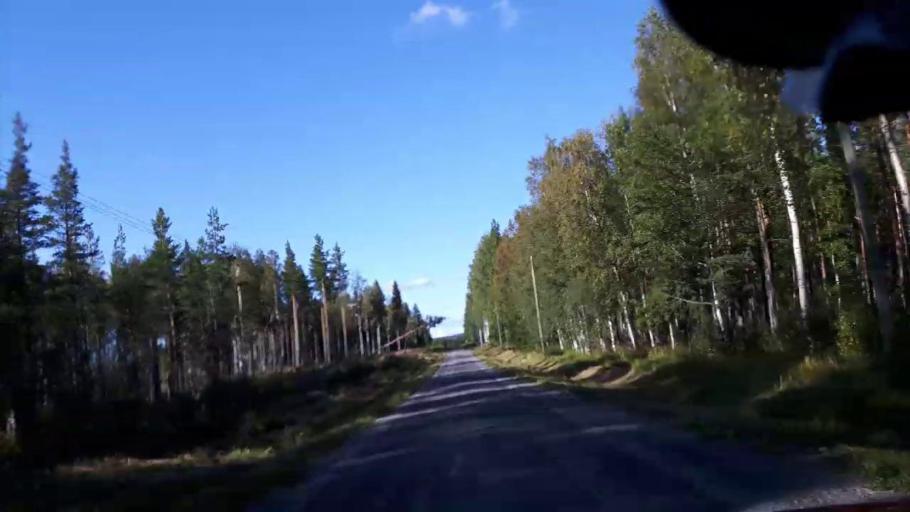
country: SE
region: Jaemtland
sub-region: Ragunda Kommun
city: Hammarstrand
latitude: 63.5183
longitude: 16.0565
